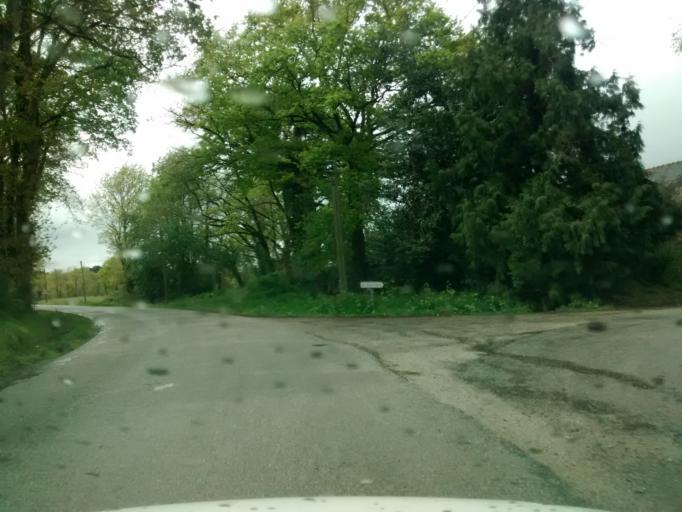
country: FR
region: Brittany
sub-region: Departement du Morbihan
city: Pleucadeuc
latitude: 47.7602
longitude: -2.3337
